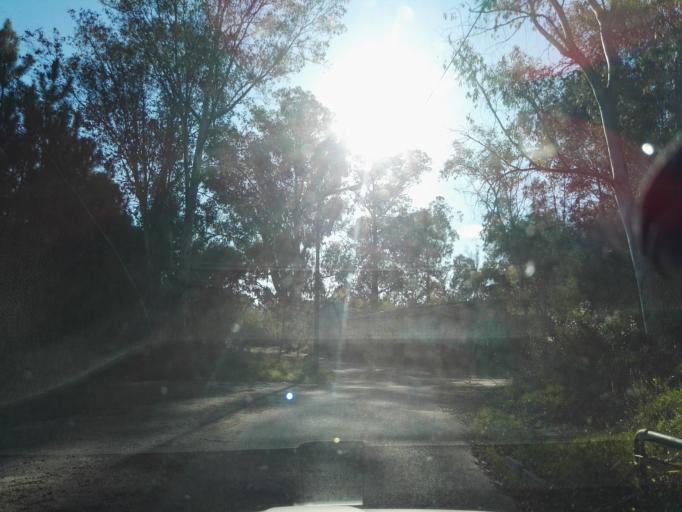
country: PT
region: Setubal
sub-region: Seixal
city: Corroios
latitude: 38.6191
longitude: -9.1466
